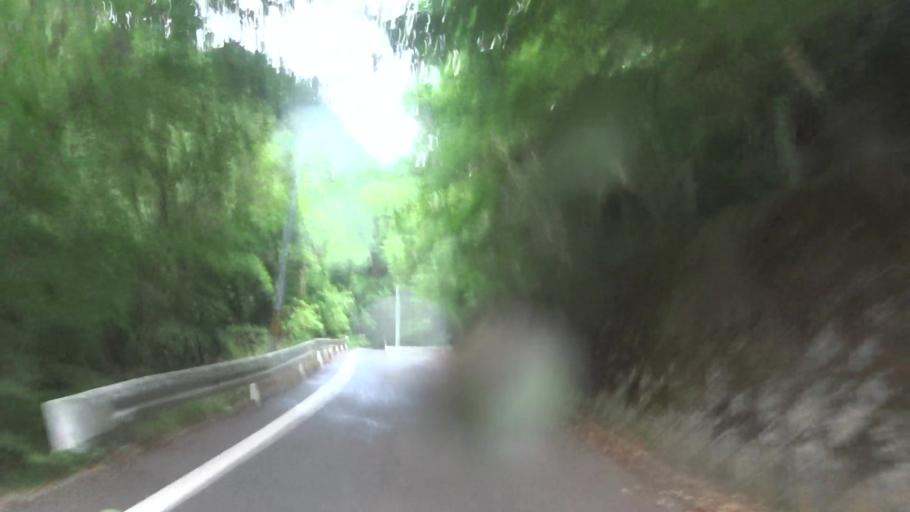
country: JP
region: Shiga Prefecture
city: Kitahama
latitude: 35.2627
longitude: 135.7921
